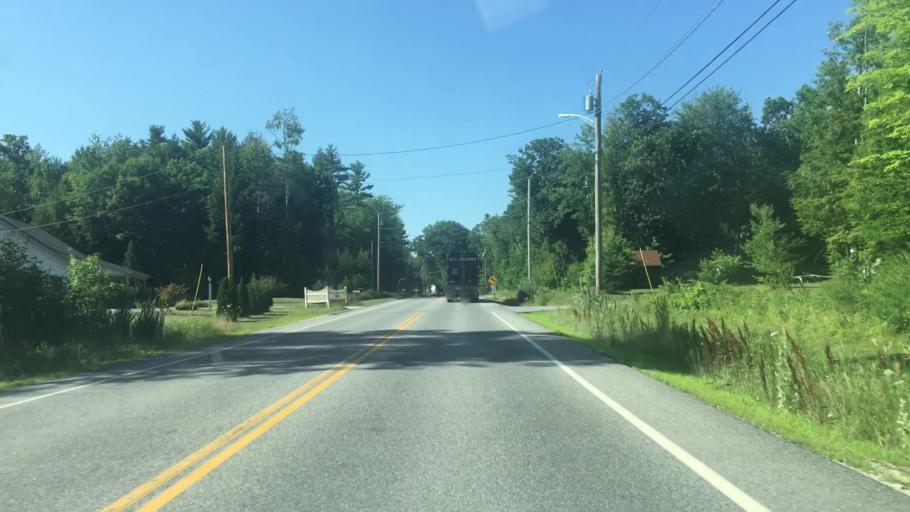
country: US
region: Maine
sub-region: York County
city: Buxton
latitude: 43.5843
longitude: -70.5183
